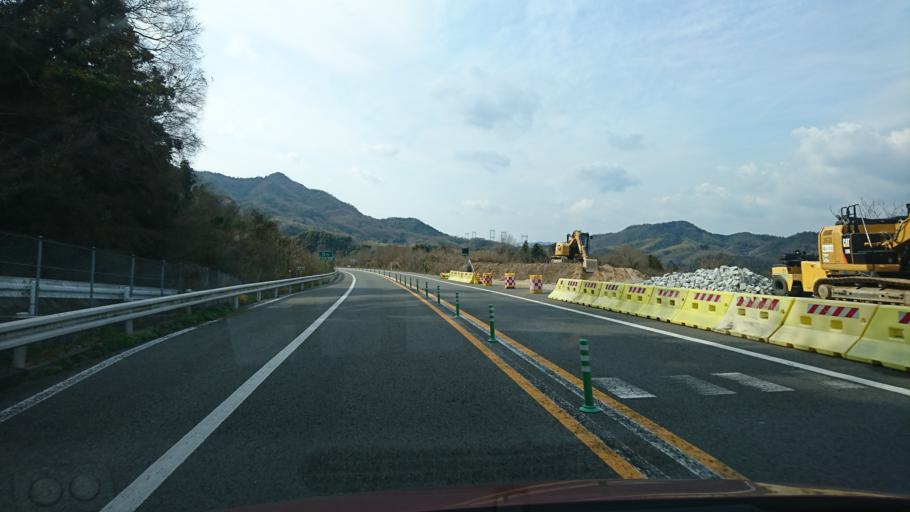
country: JP
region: Hiroshima
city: Innoshima
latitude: 34.1324
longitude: 133.0461
